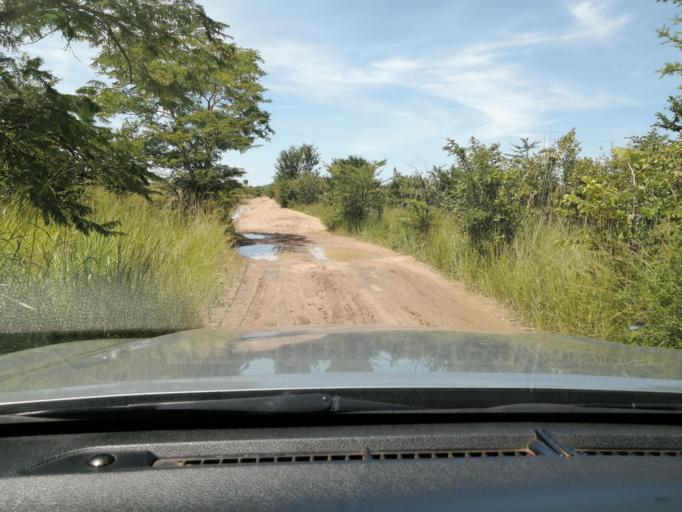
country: ZM
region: Central
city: Chibombo
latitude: -15.0548
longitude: 27.8267
